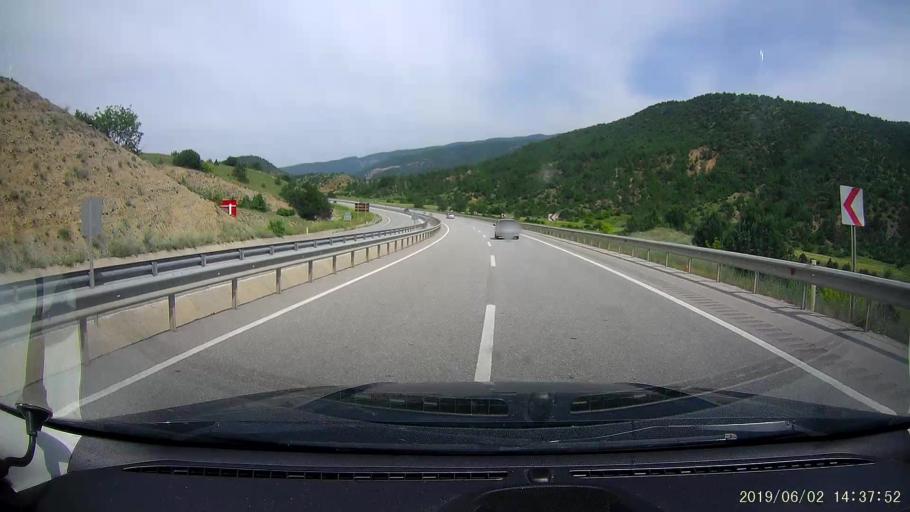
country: TR
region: Corum
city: Hacihamza
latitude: 41.0504
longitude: 34.2667
